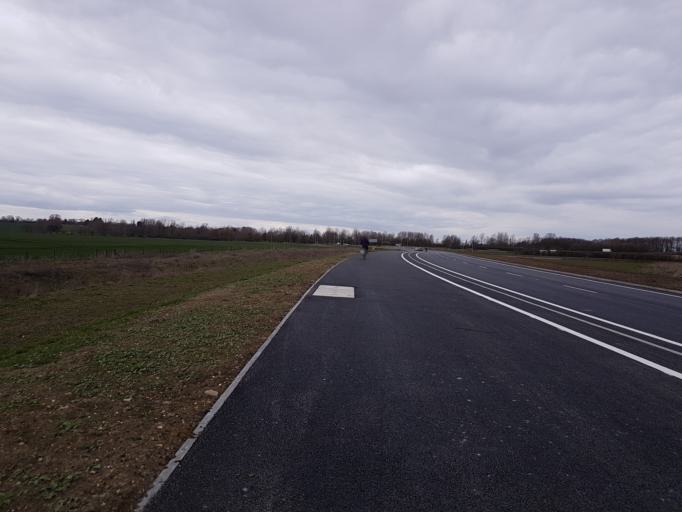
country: GB
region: England
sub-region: Cambridgeshire
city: Girton
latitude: 52.2417
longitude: 0.0438
